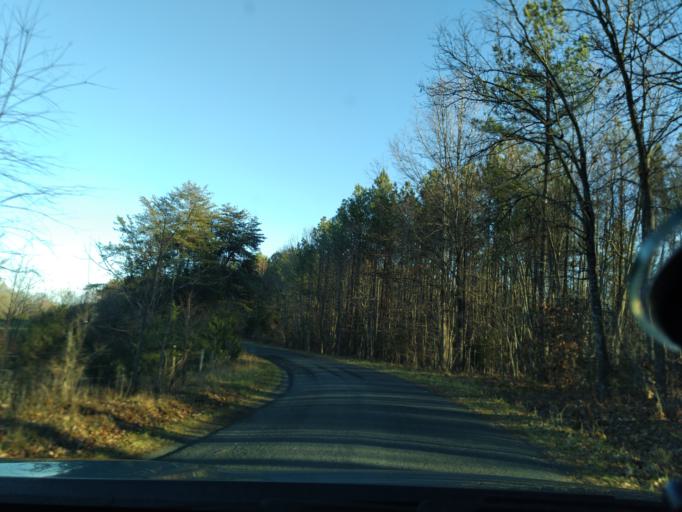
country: US
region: Virginia
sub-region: Buckingham County
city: Buckingham
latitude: 37.3659
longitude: -78.6143
